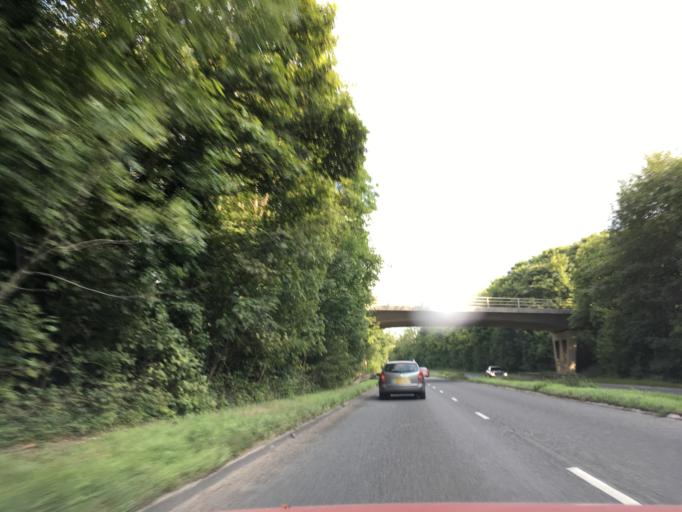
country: GB
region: England
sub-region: Gloucestershire
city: Cirencester
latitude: 51.7113
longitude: -1.9697
